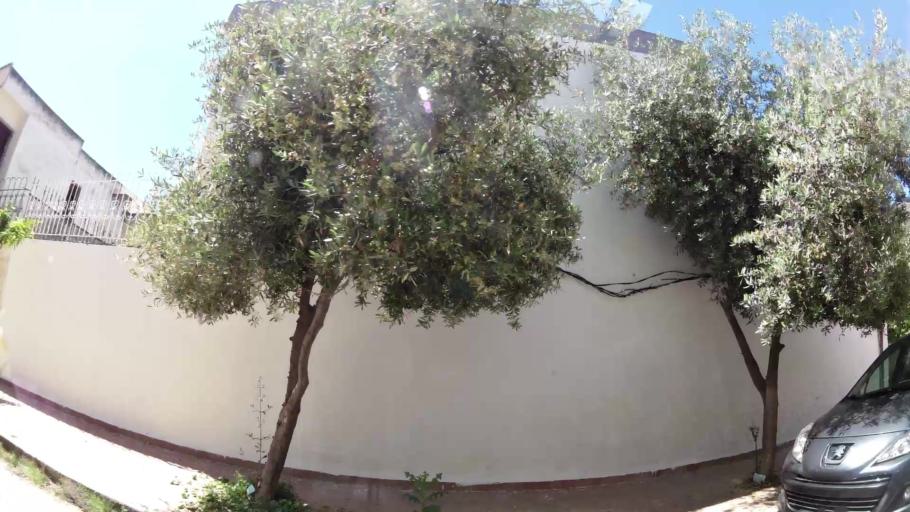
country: MA
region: Fes-Boulemane
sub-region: Fes
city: Fes
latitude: 34.0214
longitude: -5.0046
